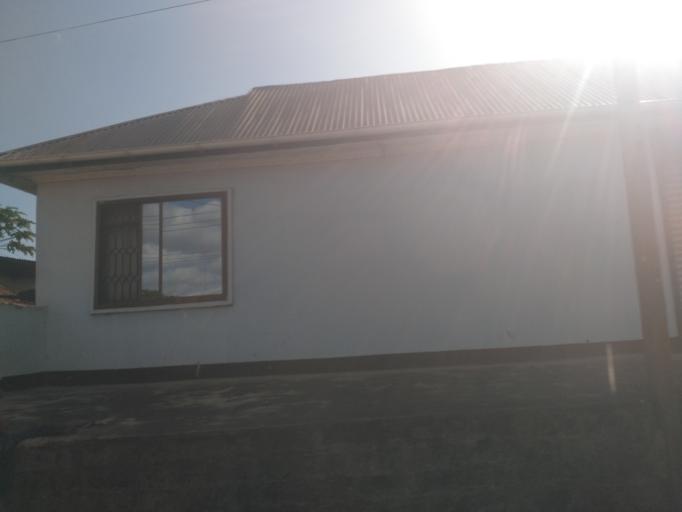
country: TZ
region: Dar es Salaam
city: Dar es Salaam
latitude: -6.8728
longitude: 39.2667
